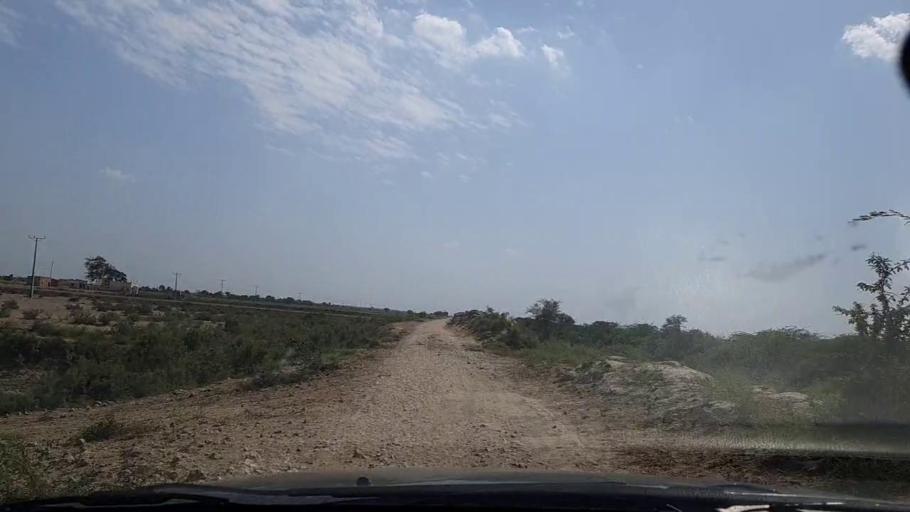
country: PK
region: Sindh
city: Mirpur Batoro
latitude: 24.5889
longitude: 68.1975
